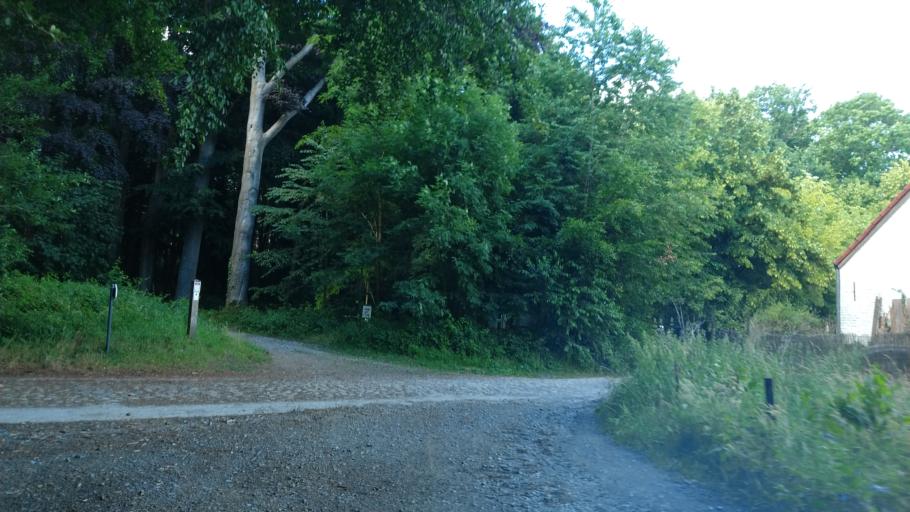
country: BE
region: Flanders
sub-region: Provincie Vlaams-Brabant
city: Bierbeek
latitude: 50.8140
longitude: 4.7480
